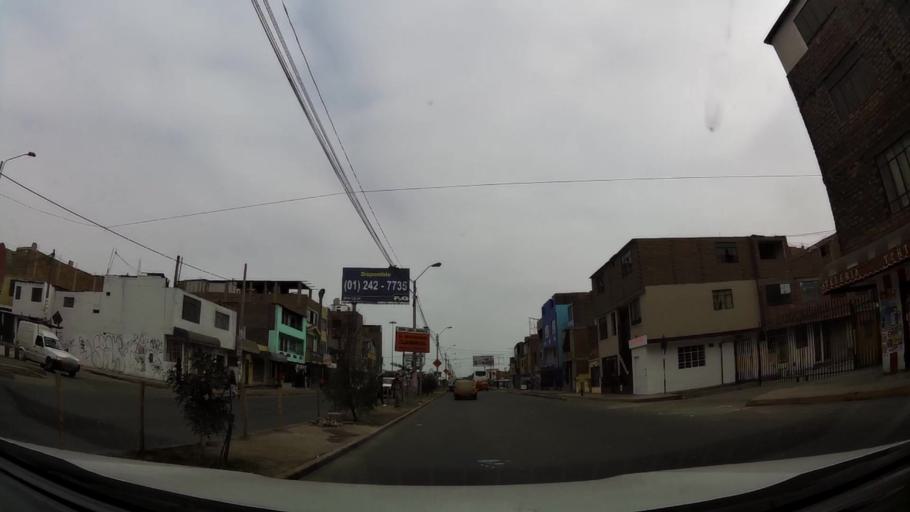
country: PE
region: Lima
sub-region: Lima
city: Independencia
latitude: -12.0247
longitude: -77.0748
